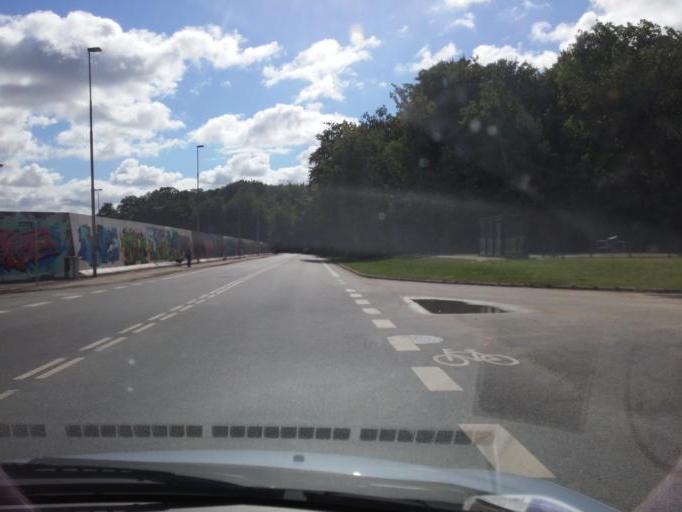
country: DK
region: South Denmark
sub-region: Odense Kommune
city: Odense
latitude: 55.4095
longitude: 10.3751
